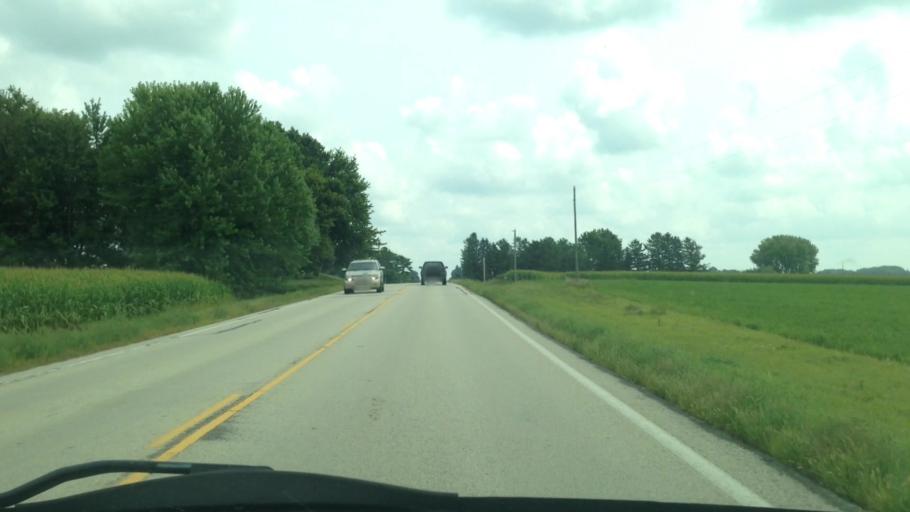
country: US
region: Minnesota
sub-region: Olmsted County
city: Rochester
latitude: 44.1369
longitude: -92.4012
